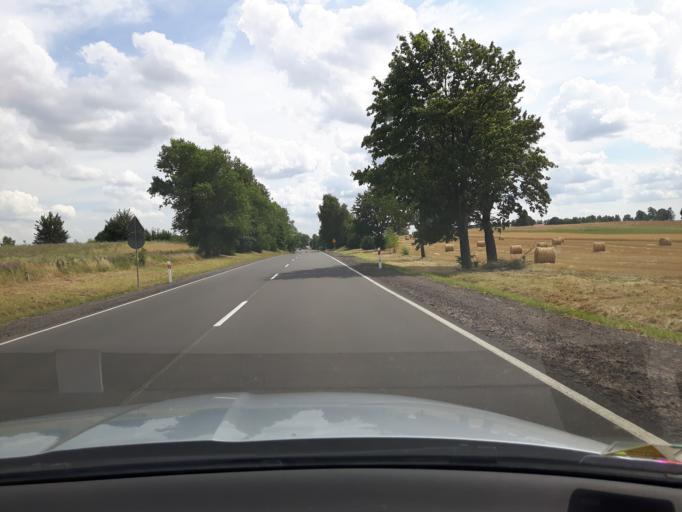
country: PL
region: Warmian-Masurian Voivodeship
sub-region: Powiat nidzicki
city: Nidzica
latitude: 53.3631
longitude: 20.3986
